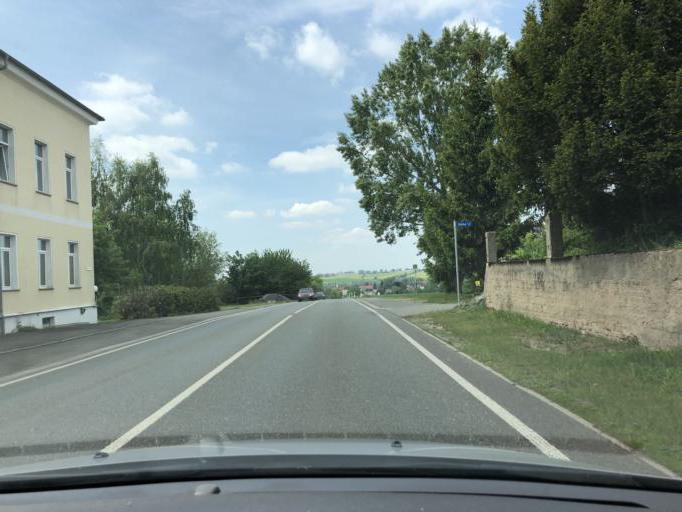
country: DE
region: Thuringia
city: Saara
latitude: 50.9301
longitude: 12.4358
